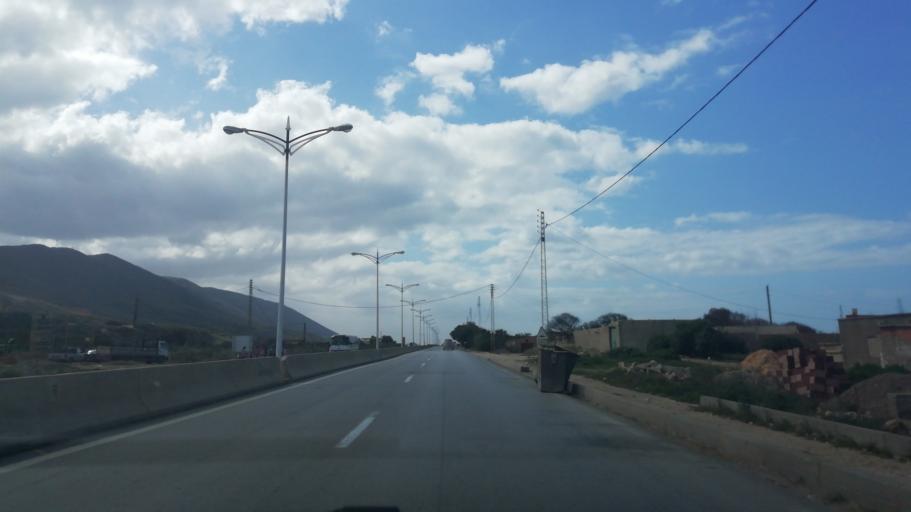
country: DZ
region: Mostaganem
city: Mostaganem
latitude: 36.0304
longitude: 0.1379
